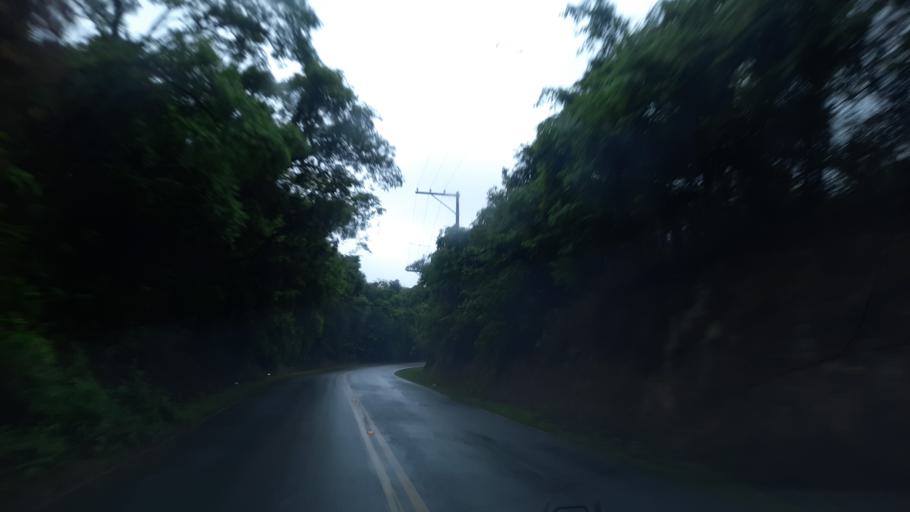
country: BR
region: Sao Paulo
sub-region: Atibaia
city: Atibaia
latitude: -23.0913
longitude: -46.5389
